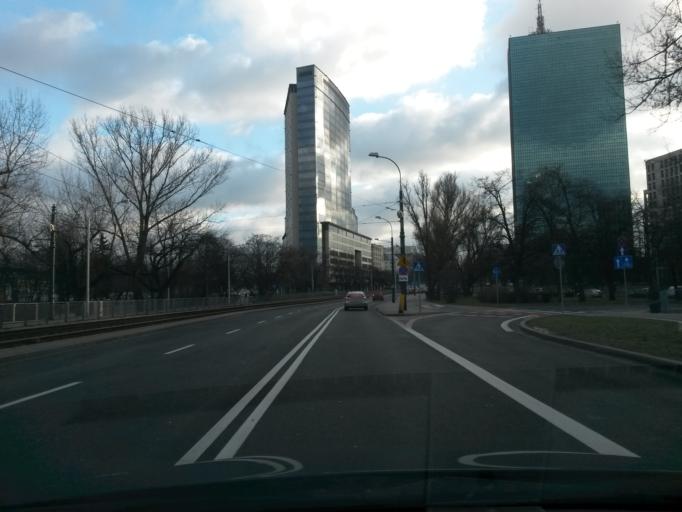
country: PL
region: Masovian Voivodeship
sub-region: Warszawa
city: Zoliborz
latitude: 52.2570
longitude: 20.9967
